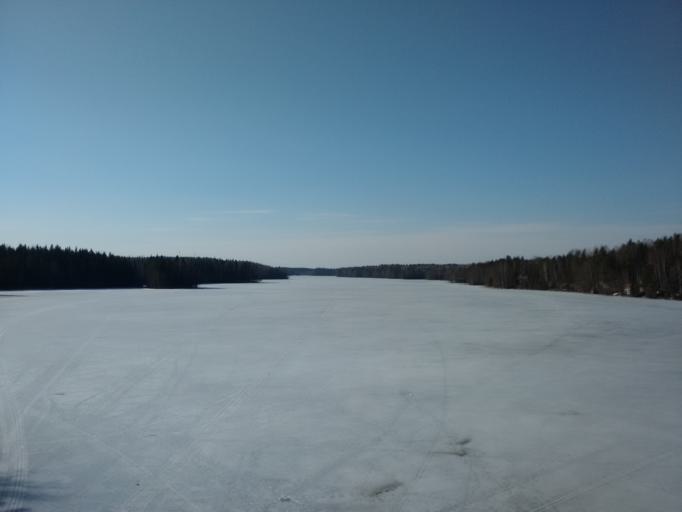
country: FI
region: Pirkanmaa
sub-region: Tampere
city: Tampere
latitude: 61.4491
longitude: 23.8055
